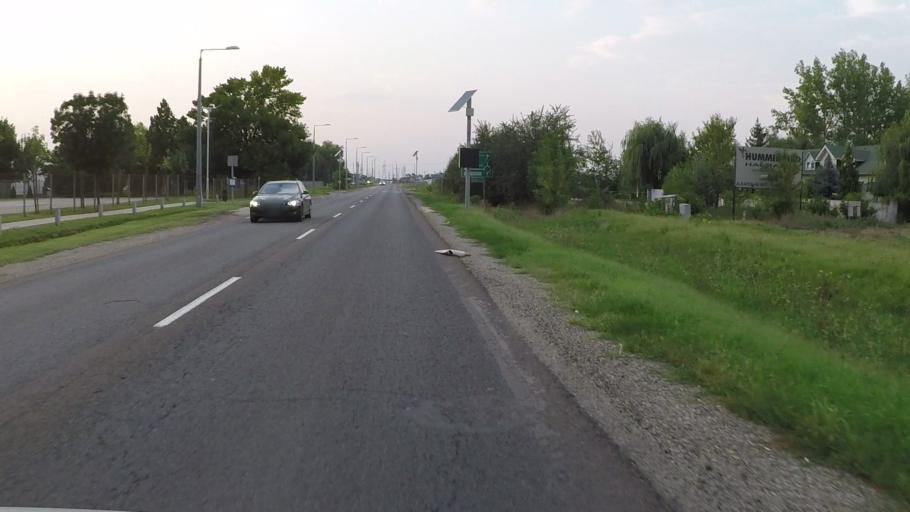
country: HU
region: Jasz-Nagykun-Szolnok
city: Szolnok
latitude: 47.1983
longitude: 20.1635
